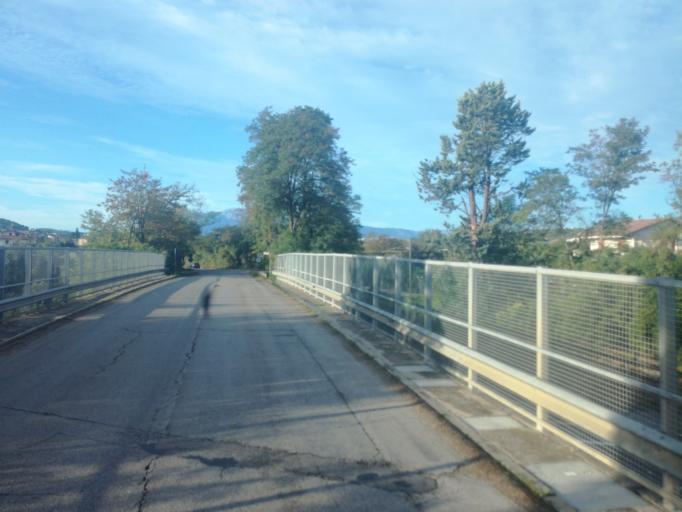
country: IT
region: Abruzzo
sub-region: Provincia di Chieti
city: Miglianico
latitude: 42.3826
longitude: 14.2902
